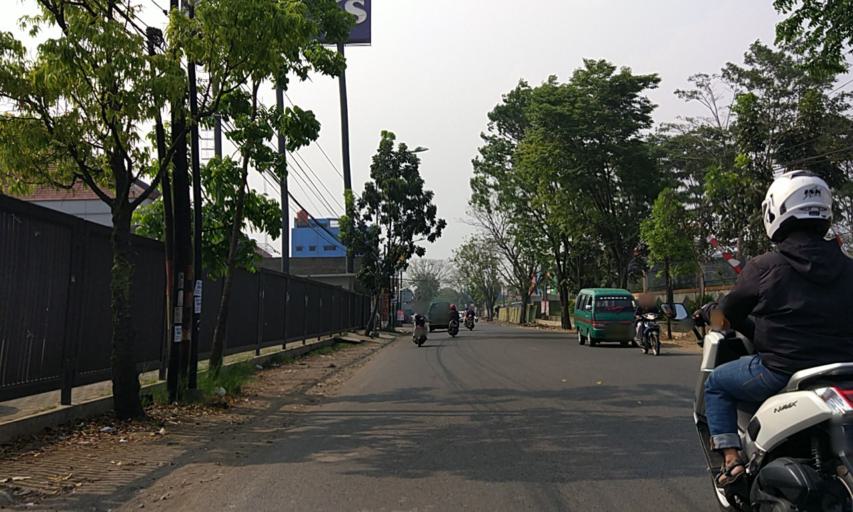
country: ID
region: West Java
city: Margahayukencana
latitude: -7.0062
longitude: 107.5516
